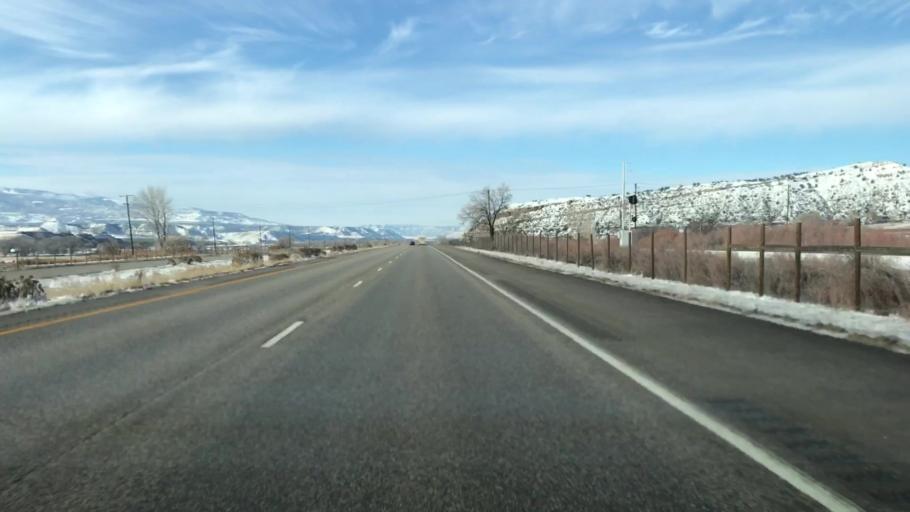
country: US
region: Colorado
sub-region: Garfield County
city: Silt
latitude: 39.5489
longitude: -107.6094
